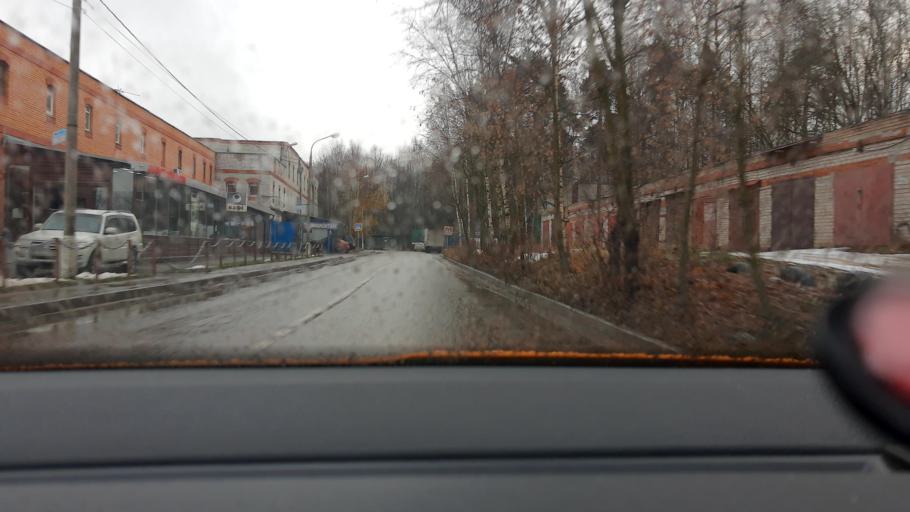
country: RU
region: Moskovskaya
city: Bolshevo
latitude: 55.9300
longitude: 37.8263
